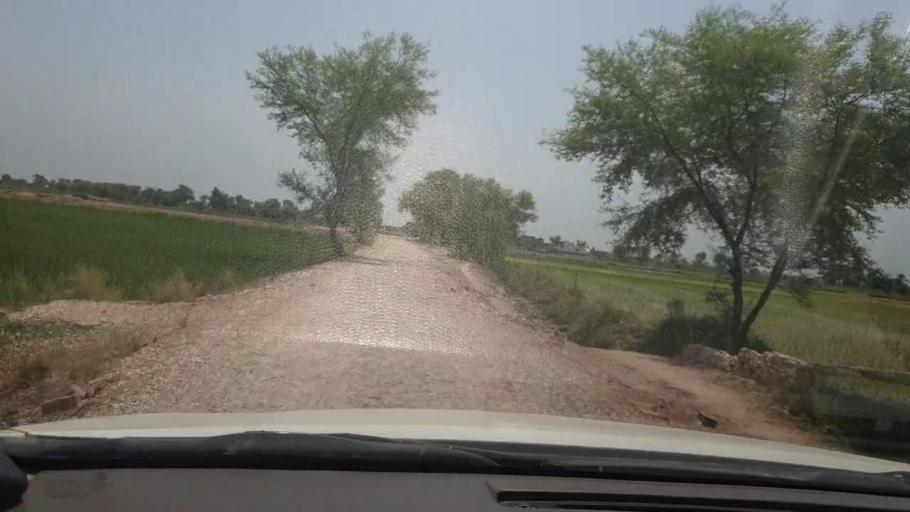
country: PK
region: Sindh
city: Garhi Yasin
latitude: 27.9143
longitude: 68.5568
